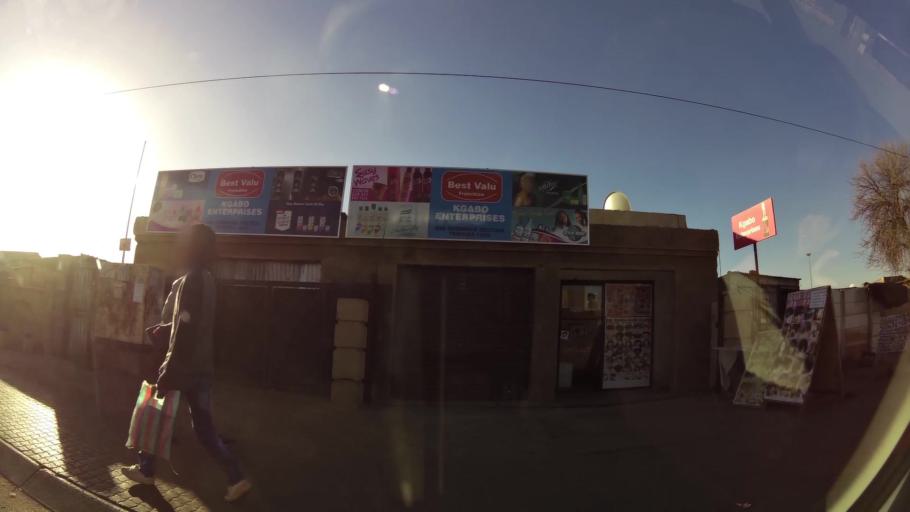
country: ZA
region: Gauteng
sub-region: Ekurhuleni Metropolitan Municipality
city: Tembisa
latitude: -26.0051
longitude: 28.2408
